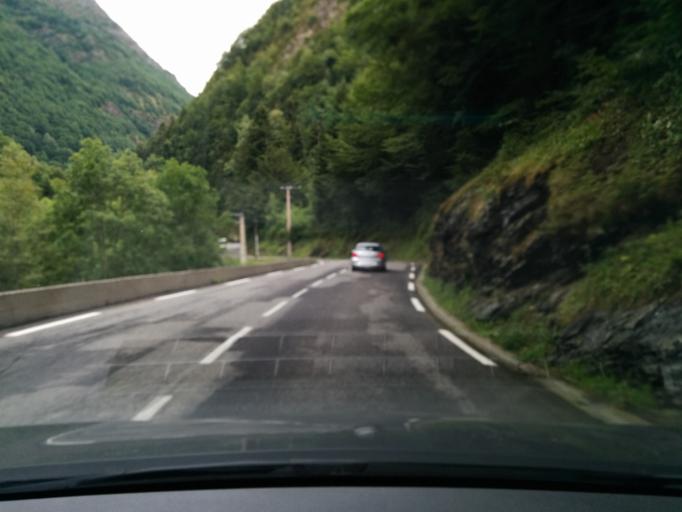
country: FR
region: Midi-Pyrenees
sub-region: Departement des Hautes-Pyrenees
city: Saint-Lary-Soulan
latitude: 42.7953
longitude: 0.2711
